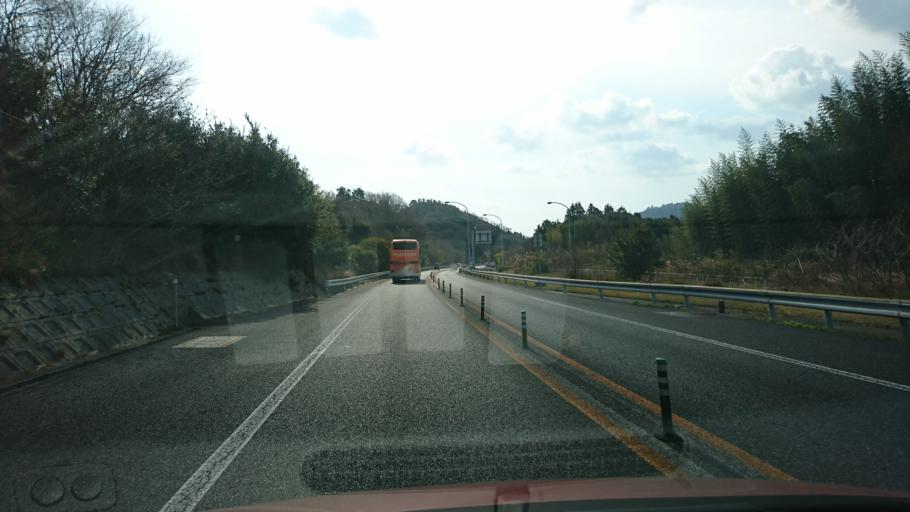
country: JP
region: Hiroshima
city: Innoshima
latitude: 34.2029
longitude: 133.0791
